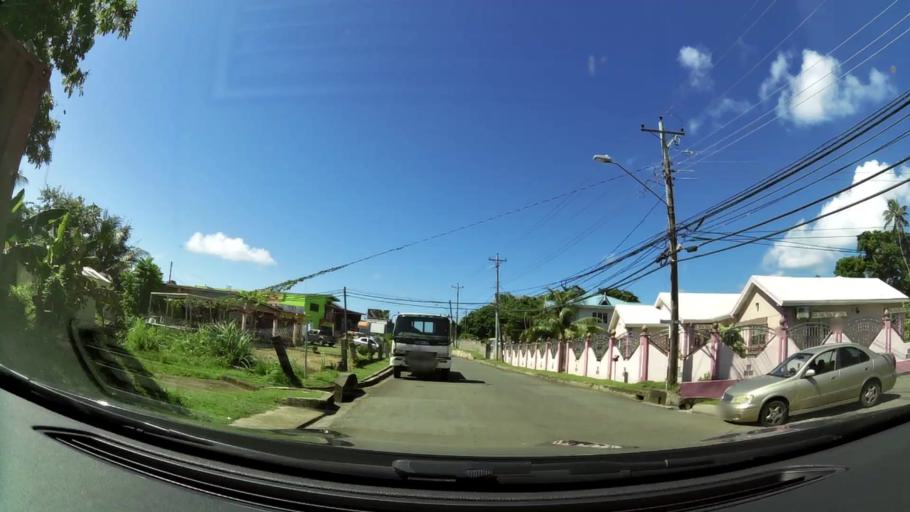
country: TT
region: Tobago
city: Scarborough
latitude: 11.1691
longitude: -60.7870
